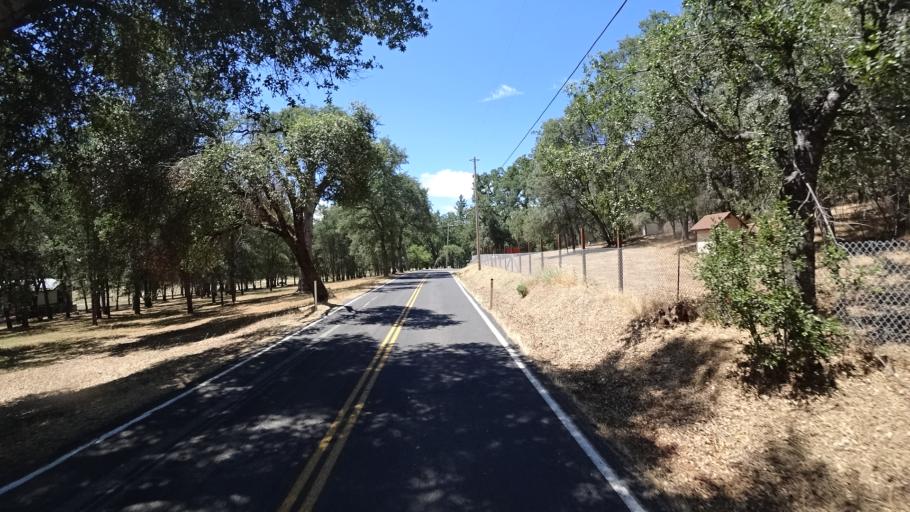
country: US
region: California
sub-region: Calaveras County
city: Mountain Ranch
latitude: 38.2257
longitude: -120.4902
